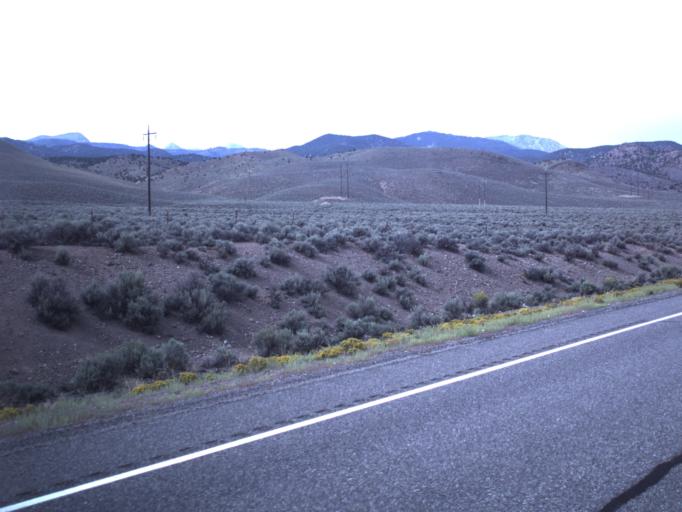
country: US
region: Utah
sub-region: Piute County
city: Junction
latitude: 38.2862
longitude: -112.2251
